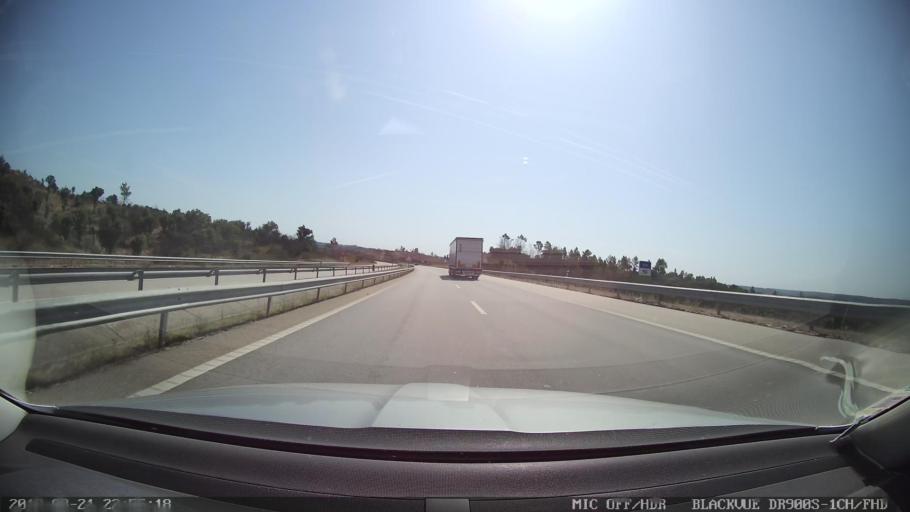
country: PT
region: Santarem
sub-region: Macao
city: Macao
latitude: 39.4929
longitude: -8.0673
